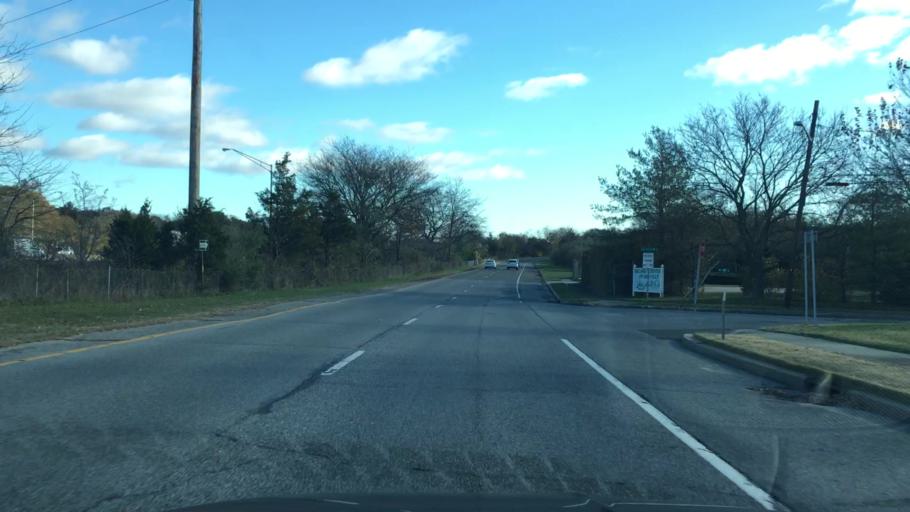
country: US
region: New York
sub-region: Suffolk County
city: Melville
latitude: 40.7831
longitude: -73.4017
